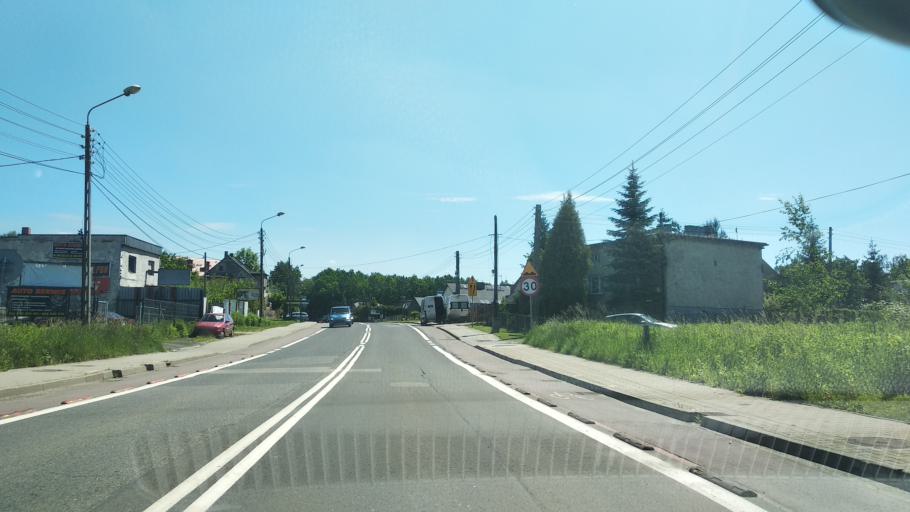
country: PL
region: Silesian Voivodeship
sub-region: Ruda Slaska
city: Ruda Slaska
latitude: 50.2391
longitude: 18.9079
